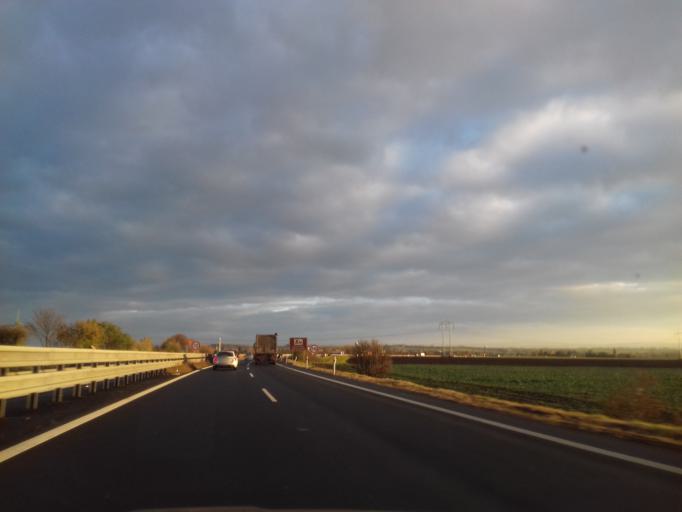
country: CZ
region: Olomoucky
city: Lutin
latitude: 49.5205
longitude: 17.1516
